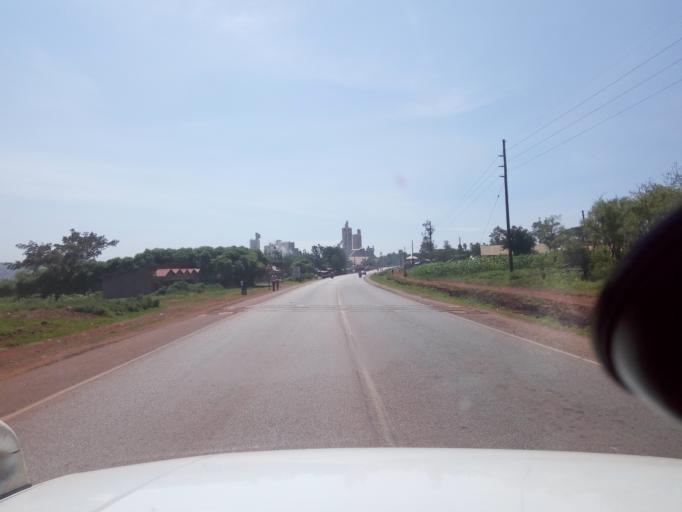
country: UG
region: Eastern Region
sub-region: Tororo District
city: Tororo
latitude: 0.6591
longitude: 34.1481
